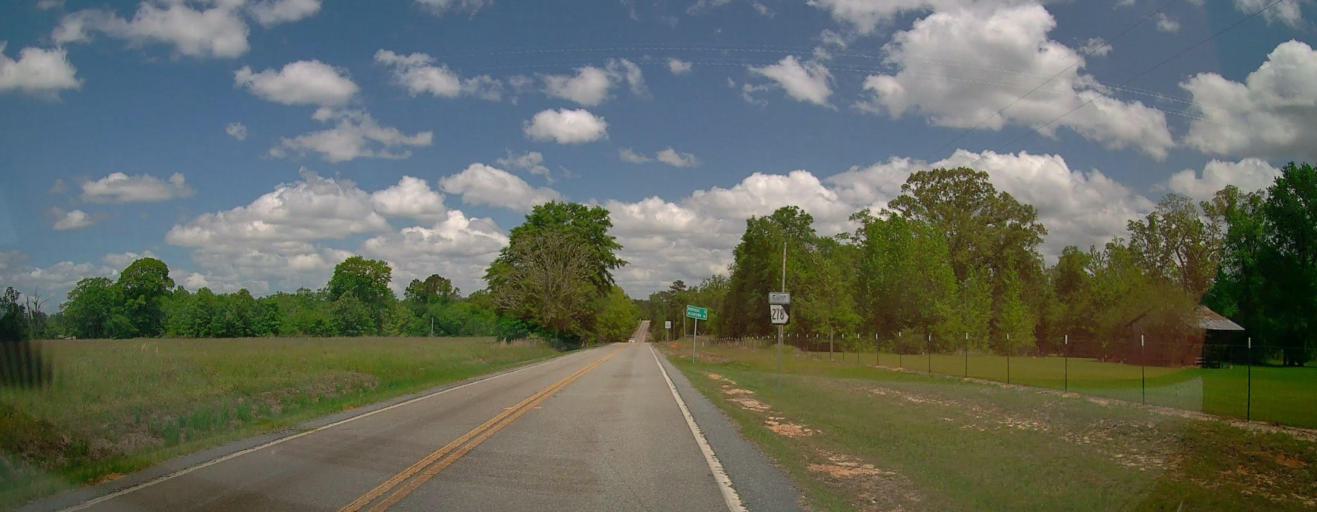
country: US
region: Georgia
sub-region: Bleckley County
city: Cochran
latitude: 32.4510
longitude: -83.2870
